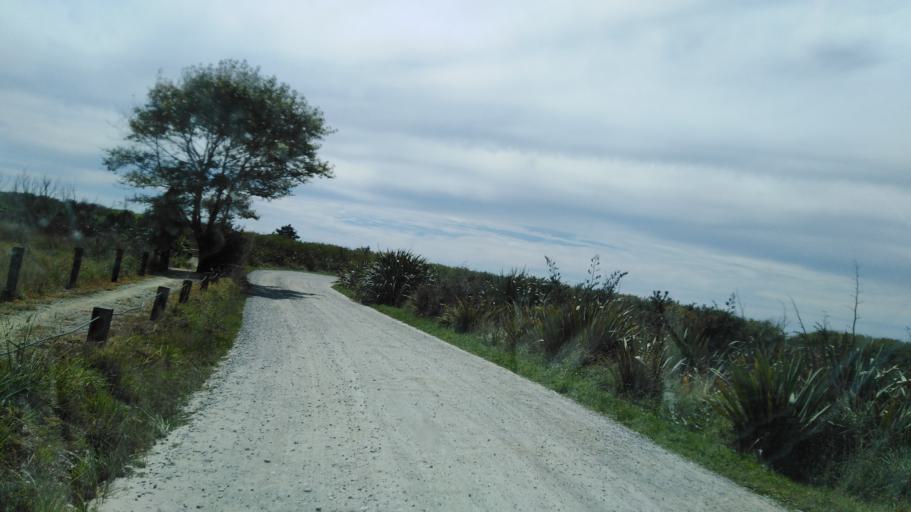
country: NZ
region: West Coast
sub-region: Buller District
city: Westport
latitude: -41.7374
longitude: 171.6043
